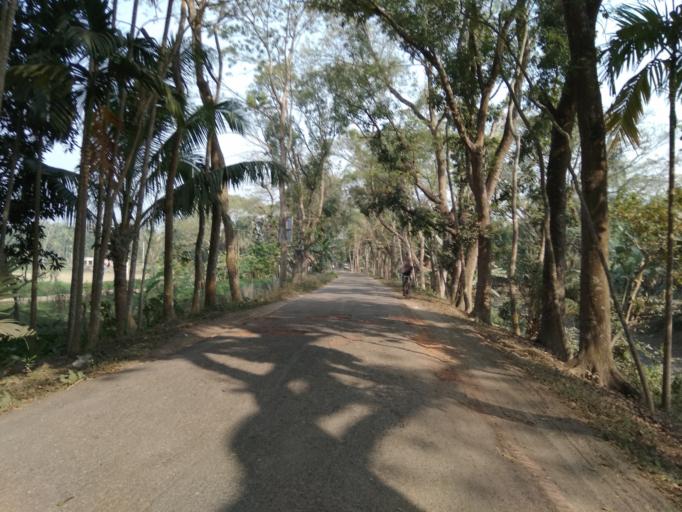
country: BD
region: Barisal
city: Mehendiganj
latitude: 22.9600
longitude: 90.4150
